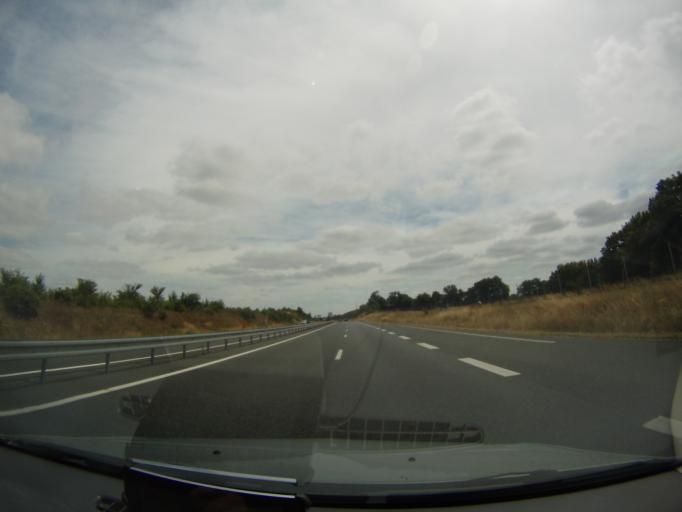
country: FR
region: Pays de la Loire
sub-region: Departement de Maine-et-Loire
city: La Tessoualle
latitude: 46.9881
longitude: -0.8429
